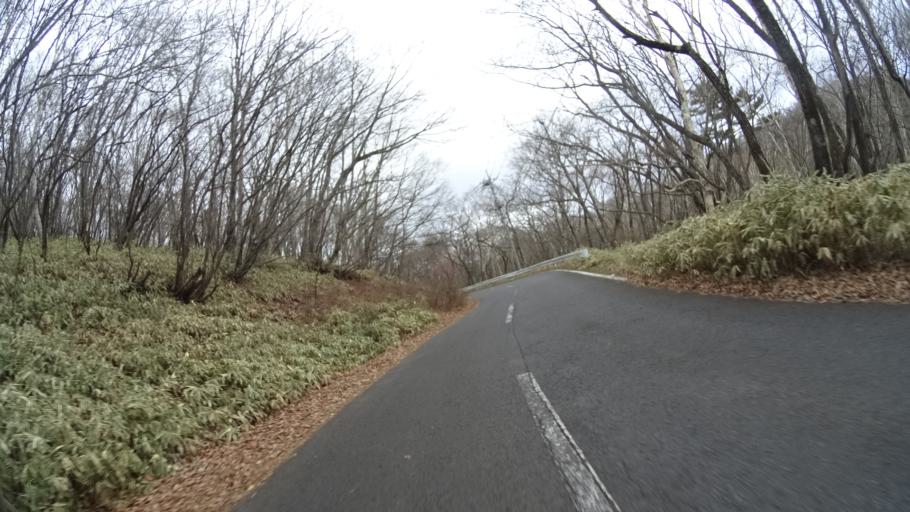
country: JP
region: Gunma
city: Omamacho-omama
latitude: 36.5359
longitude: 139.1790
